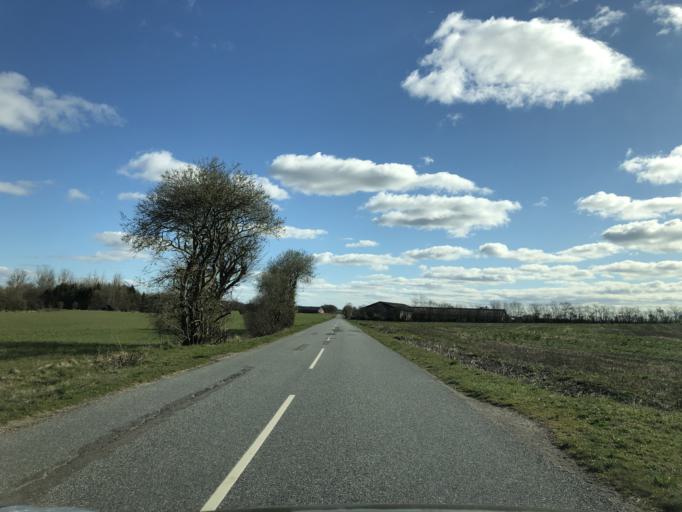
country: DK
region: North Denmark
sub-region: Vesthimmerland Kommune
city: Alestrup
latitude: 56.6109
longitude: 9.5992
